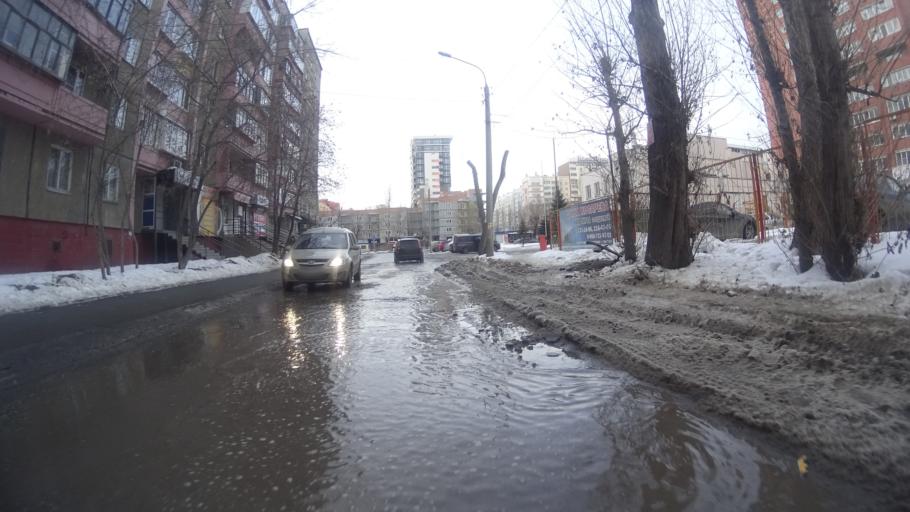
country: RU
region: Chelyabinsk
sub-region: Gorod Chelyabinsk
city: Chelyabinsk
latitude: 55.1776
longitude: 61.3469
